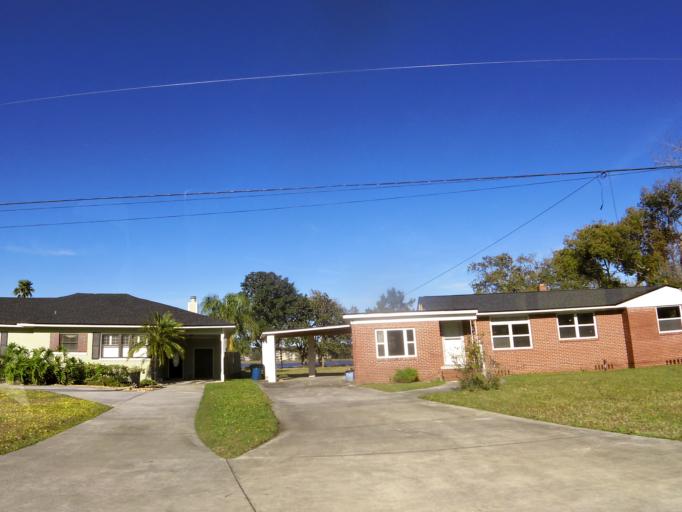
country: US
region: Florida
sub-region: Duval County
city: Jacksonville
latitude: 30.4026
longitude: -81.6723
